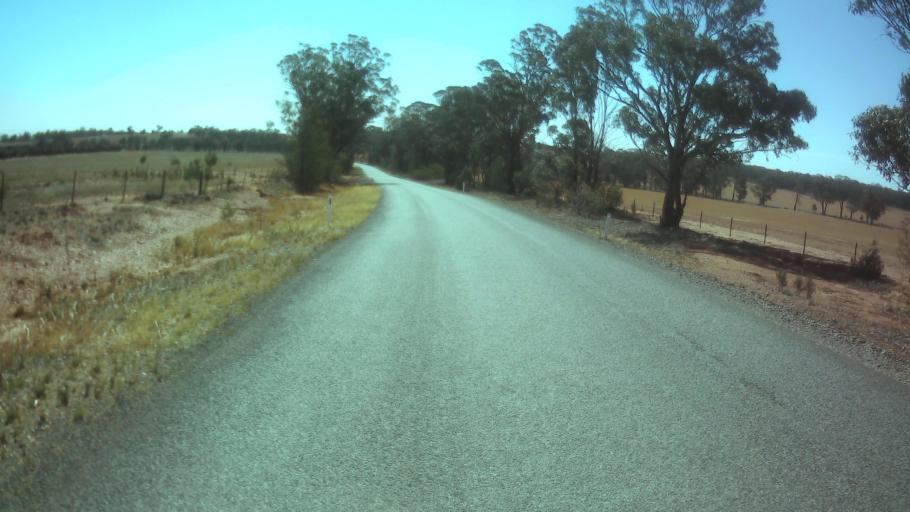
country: AU
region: New South Wales
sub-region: Weddin
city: Grenfell
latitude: -33.7550
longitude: 147.8515
